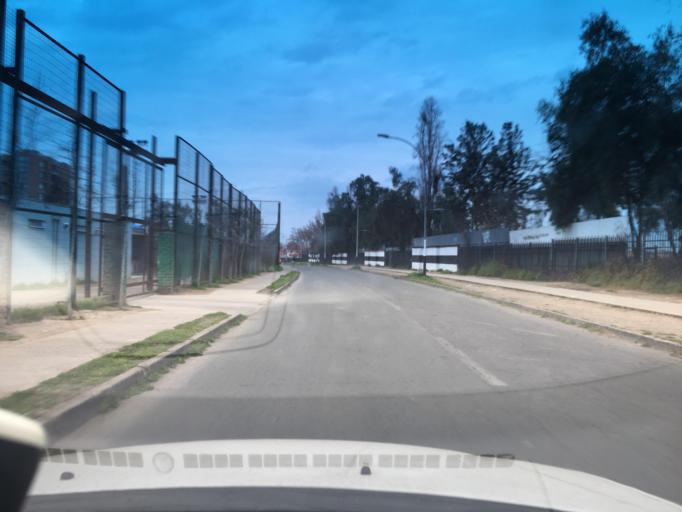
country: CL
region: Santiago Metropolitan
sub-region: Provincia de Santiago
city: Villa Presidente Frei, Nunoa, Santiago, Chile
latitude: -33.5036
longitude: -70.6061
